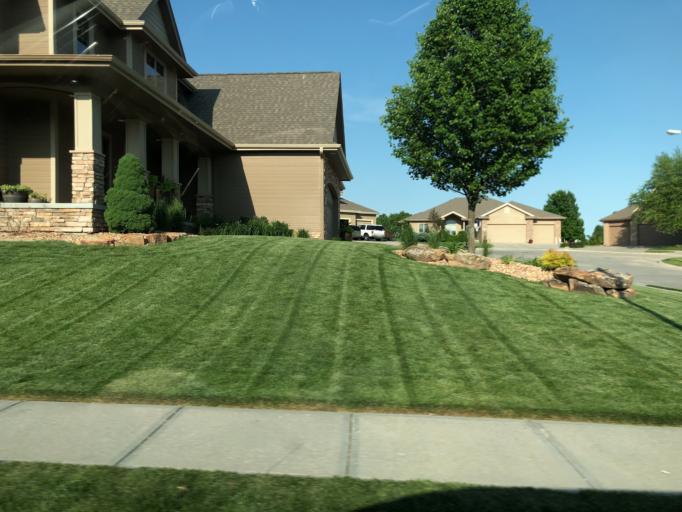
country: US
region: Nebraska
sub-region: Douglas County
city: Elkhorn
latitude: 41.2807
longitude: -96.1883
